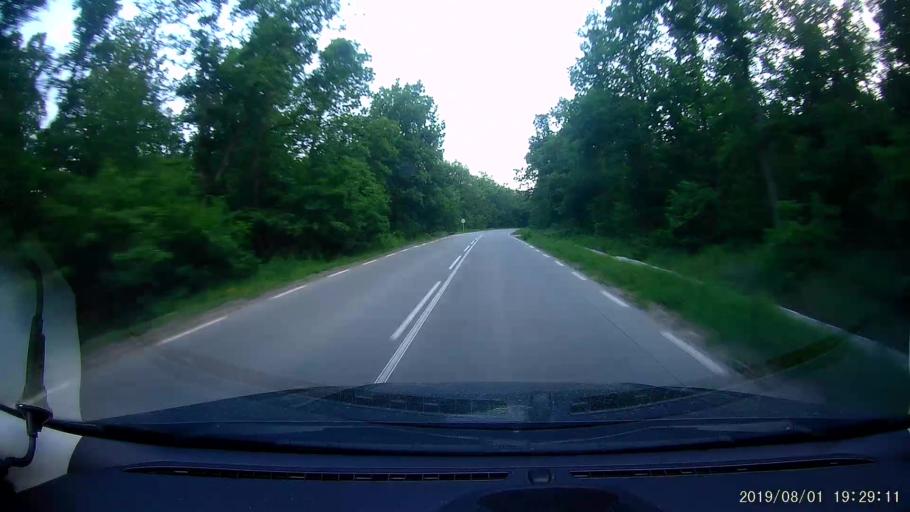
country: BG
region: Burgas
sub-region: Obshtina Sungurlare
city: Sungurlare
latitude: 42.8300
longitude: 26.9097
